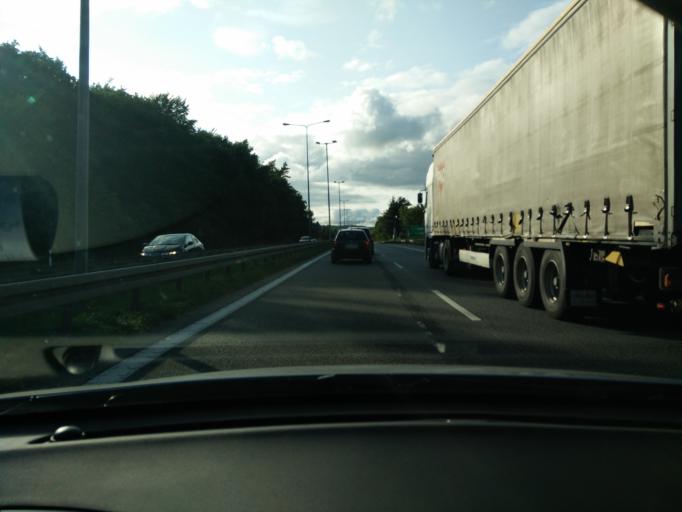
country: PL
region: Pomeranian Voivodeship
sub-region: Gdynia
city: Wielki Kack
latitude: 54.4662
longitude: 18.4803
